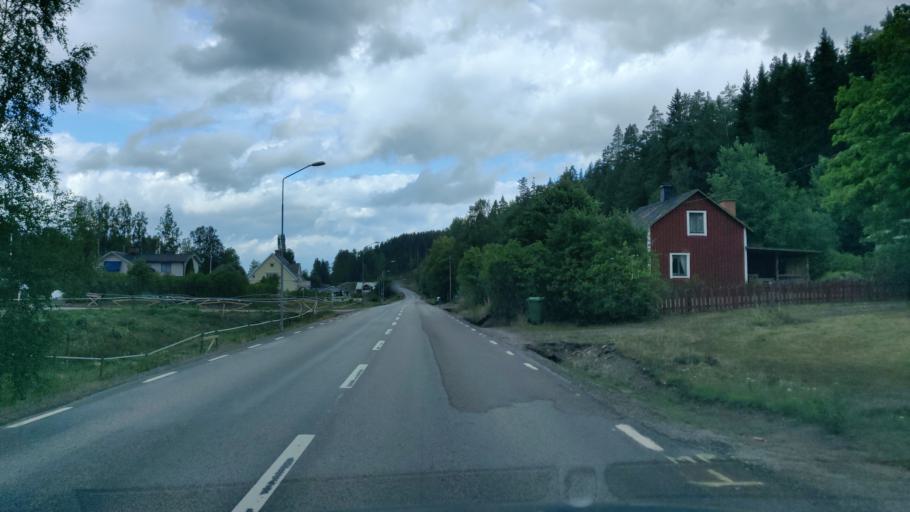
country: SE
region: Vaermland
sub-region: Torsby Kommun
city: Torsby
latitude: 60.6176
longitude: 13.0396
